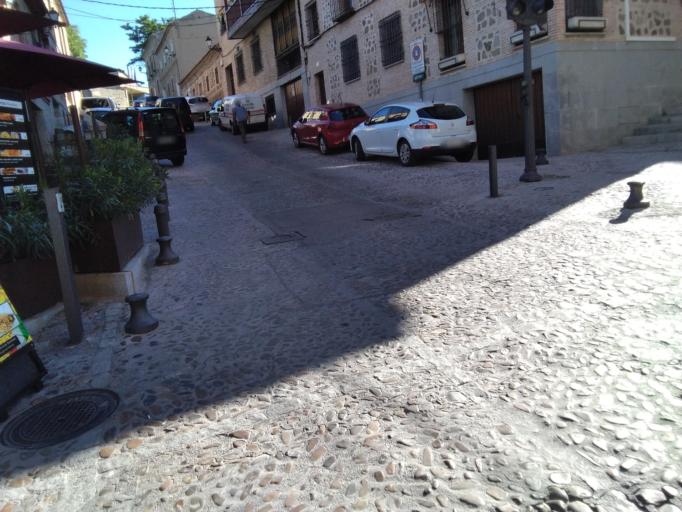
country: ES
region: Castille-La Mancha
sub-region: Province of Toledo
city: Toledo
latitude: 39.8582
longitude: -4.0315
